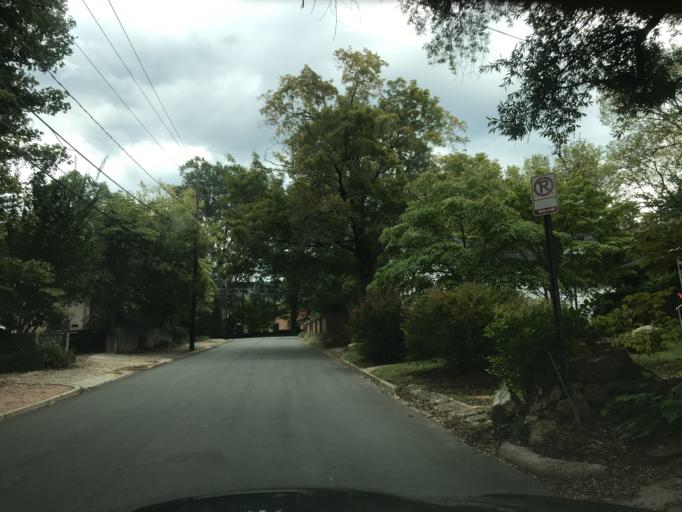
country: US
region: North Carolina
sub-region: Orange County
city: Chapel Hill
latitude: 35.9099
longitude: -79.0585
